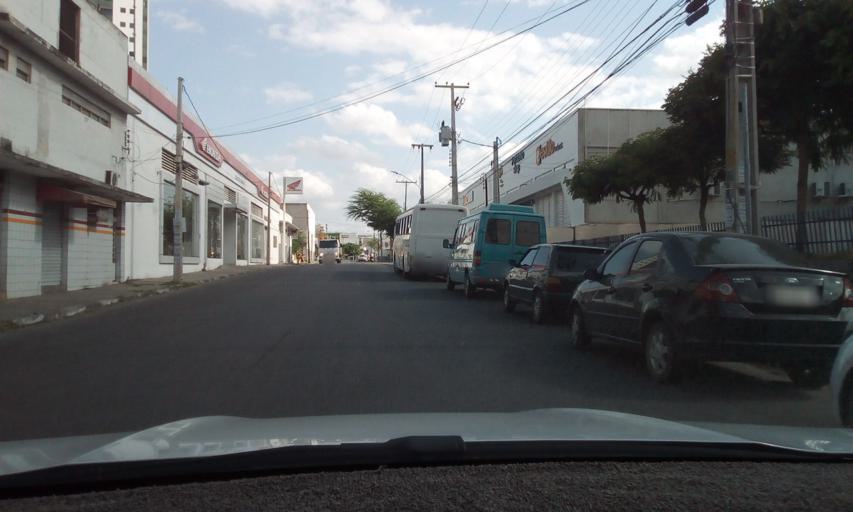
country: BR
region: Pernambuco
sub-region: Caruaru
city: Caruaru
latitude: -8.2729
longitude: -35.9756
